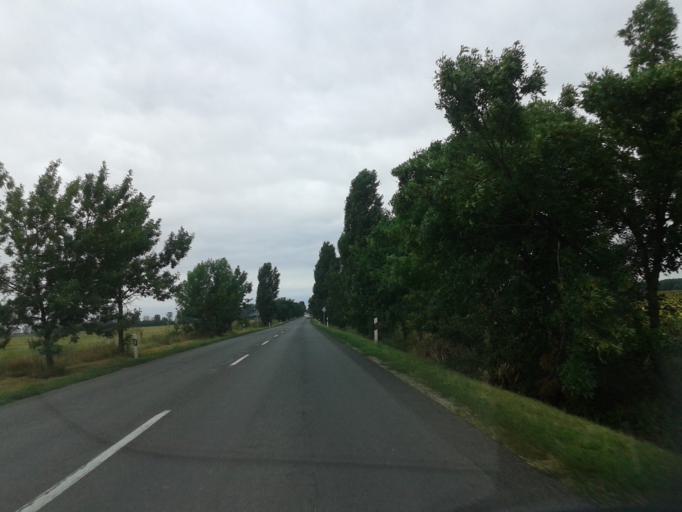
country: HU
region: Pest
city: Dunavarsany
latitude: 47.2576
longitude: 19.0262
